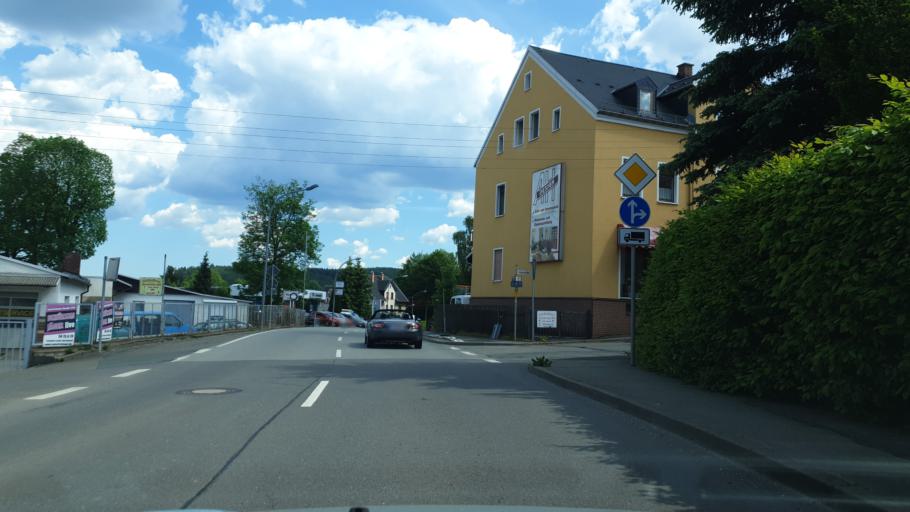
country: DE
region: Saxony
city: Lauter
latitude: 50.5602
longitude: 12.7314
